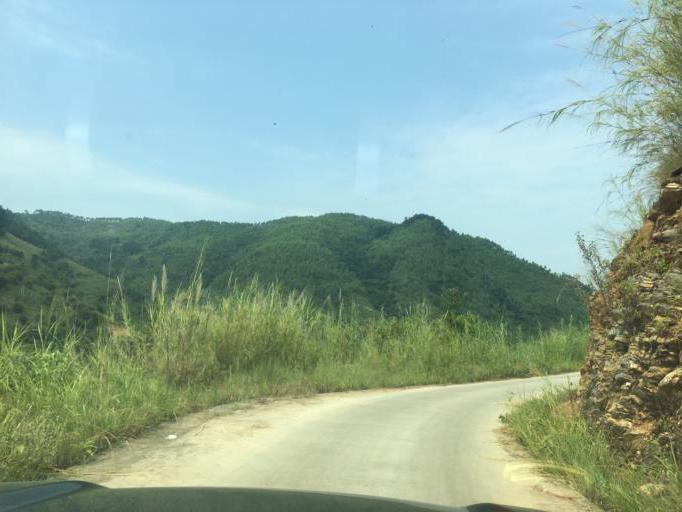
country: CN
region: Guizhou Sheng
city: Anshun
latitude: 25.4277
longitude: 105.9610
